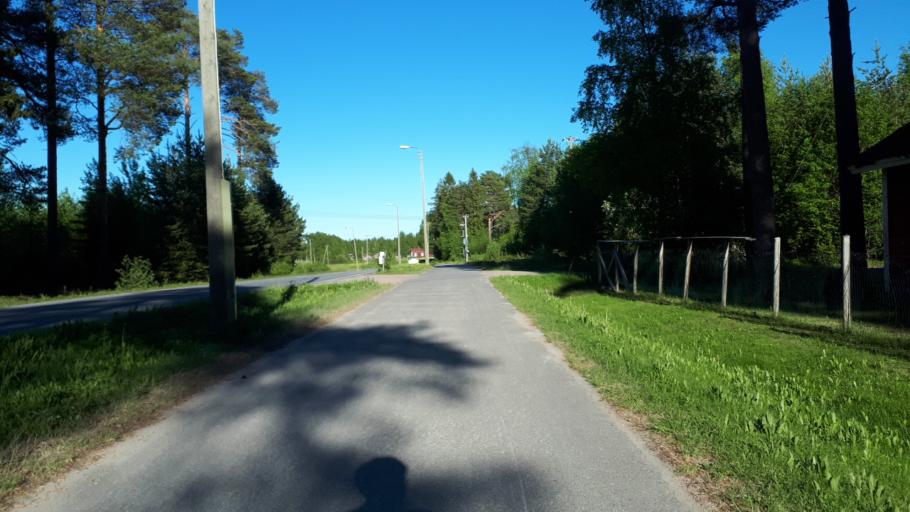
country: FI
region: Northern Ostrobothnia
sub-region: Oulunkaari
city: Ii
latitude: 65.3241
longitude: 25.4849
